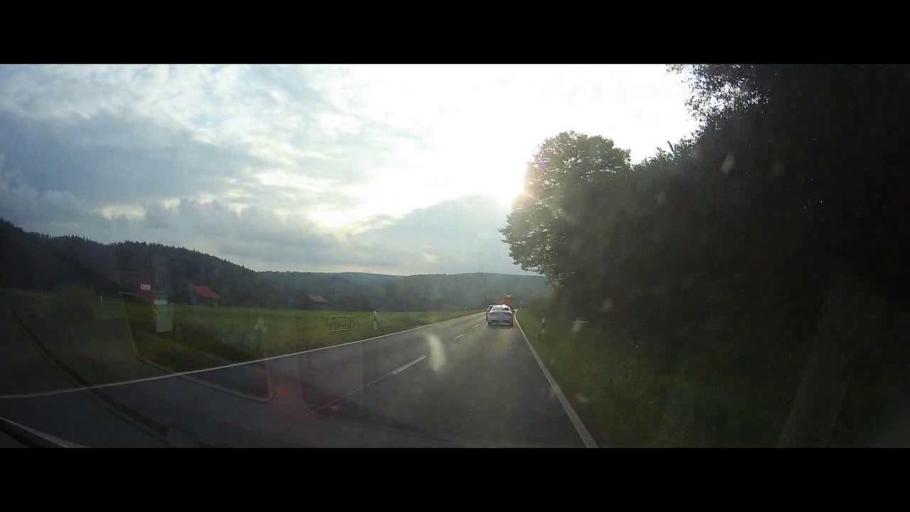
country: DE
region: Lower Saxony
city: Adelebsen
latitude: 51.5639
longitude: 9.7655
